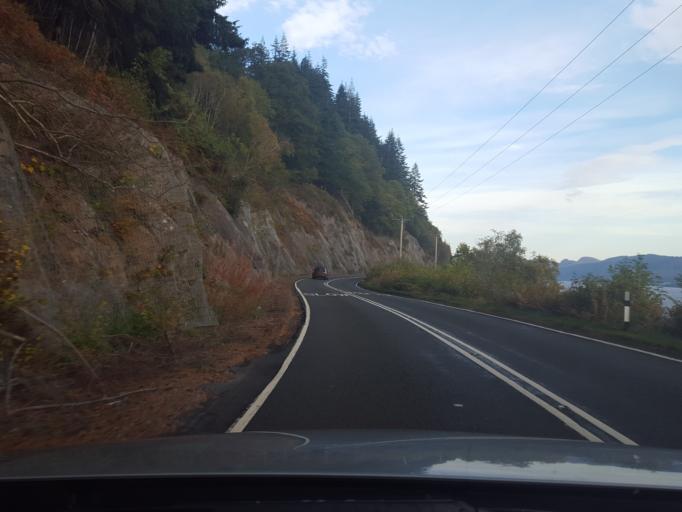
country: GB
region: Scotland
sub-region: Highland
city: Beauly
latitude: 57.2444
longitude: -4.5445
